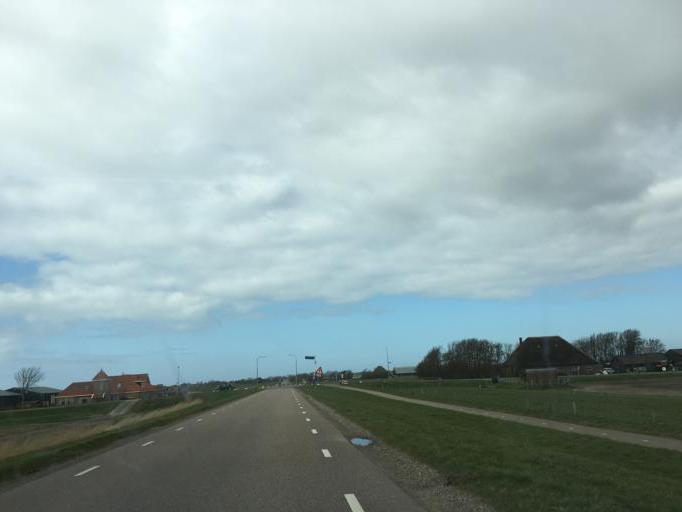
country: NL
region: North Holland
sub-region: Gemeente Schagen
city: Schagen
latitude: 52.8526
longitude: 4.7355
